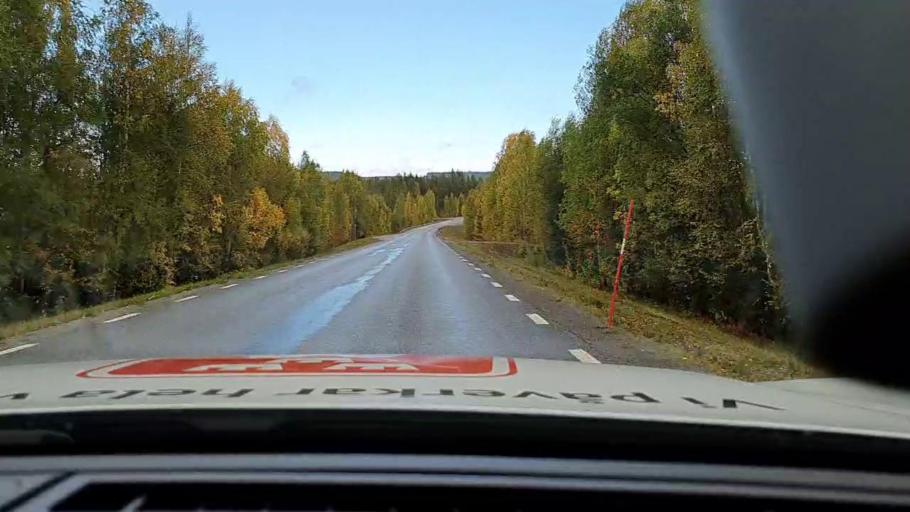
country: SE
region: Vaesterbotten
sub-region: Norsjo Kommun
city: Norsjoe
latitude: 64.9604
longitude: 19.6947
